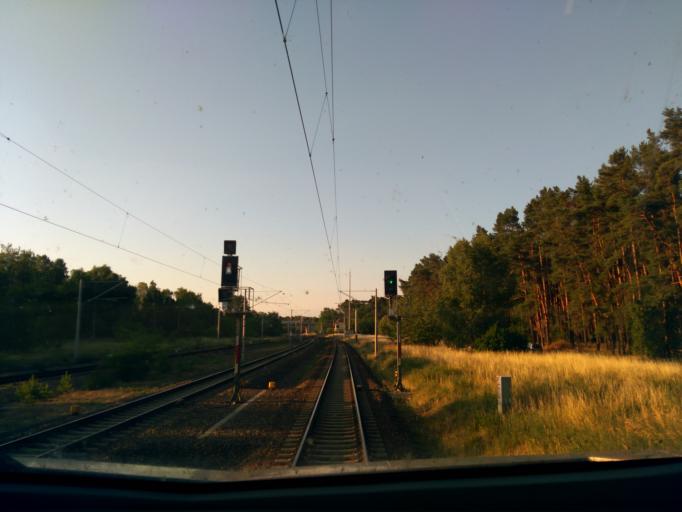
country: DE
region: Brandenburg
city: Halbe
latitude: 52.0291
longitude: 13.7220
